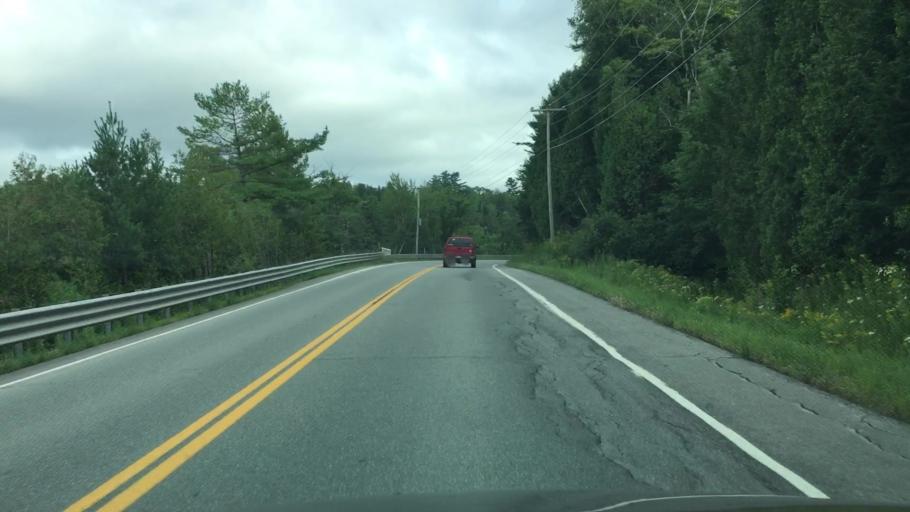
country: US
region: Maine
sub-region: Waldo County
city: Frankfort
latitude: 44.6029
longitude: -68.8690
